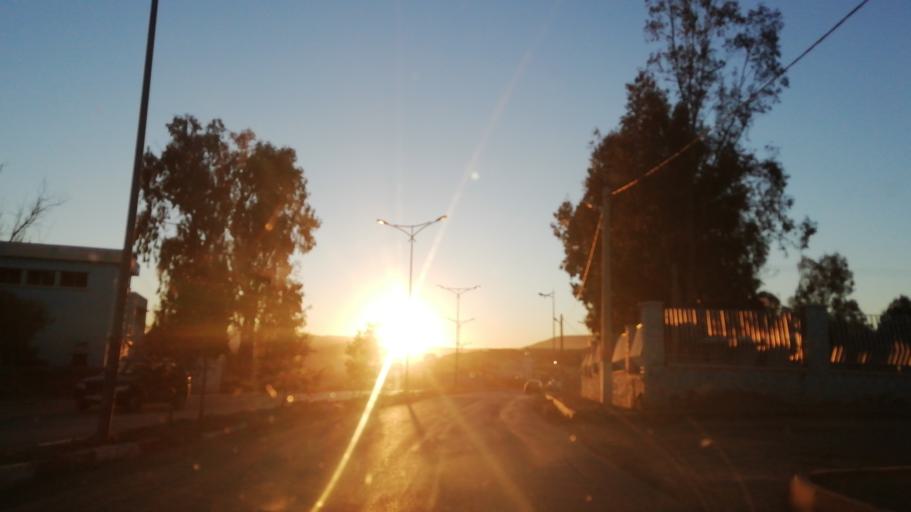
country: DZ
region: Saida
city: Saida
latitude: 34.8346
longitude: 0.1712
